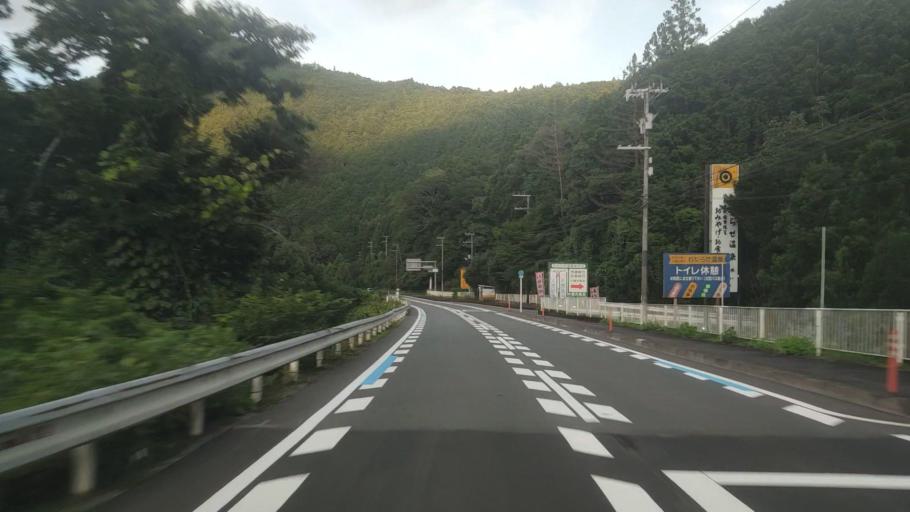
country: JP
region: Wakayama
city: Shingu
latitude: 33.8175
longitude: 135.7634
